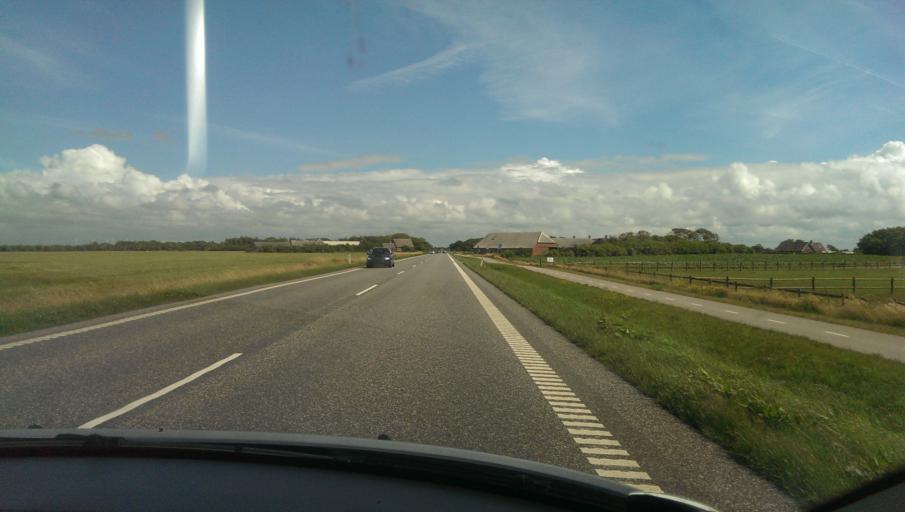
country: DK
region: Central Jutland
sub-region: Ringkobing-Skjern Kommune
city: Ringkobing
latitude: 56.1080
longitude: 8.2018
